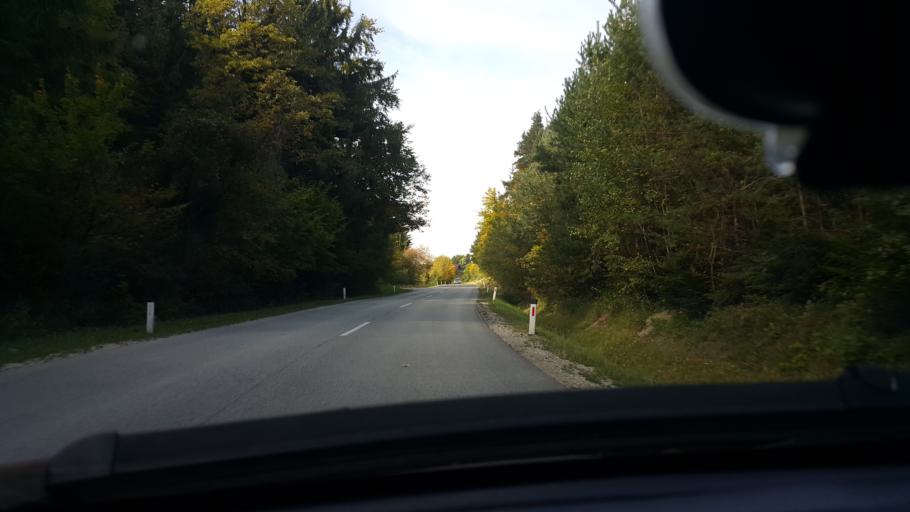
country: SI
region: Zrece
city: Zrece
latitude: 46.3731
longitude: 15.3402
